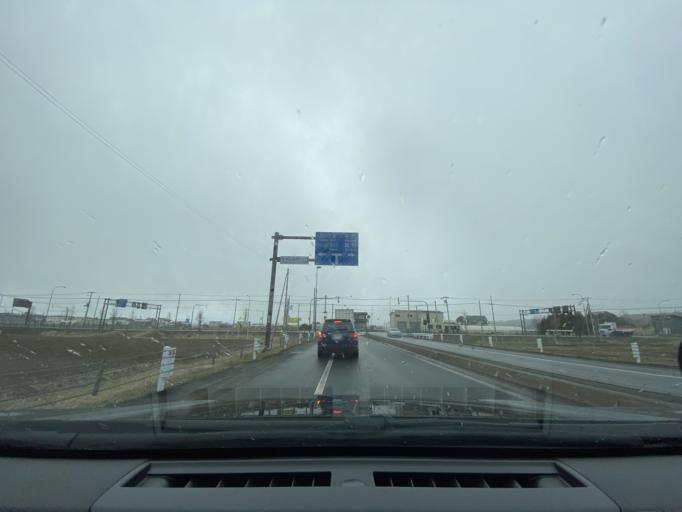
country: JP
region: Hokkaido
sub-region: Asahikawa-shi
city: Asahikawa
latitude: 43.8345
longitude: 142.4061
